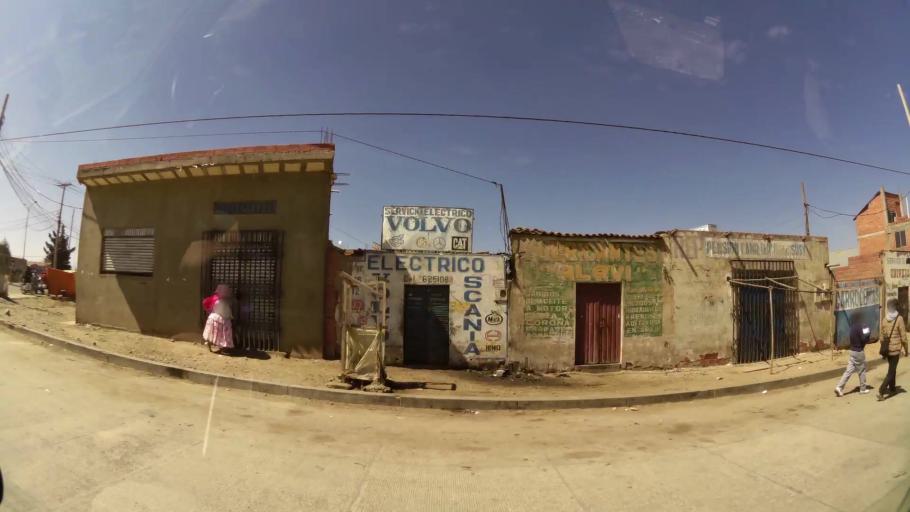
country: BO
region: La Paz
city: La Paz
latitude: -16.5439
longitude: -68.1786
